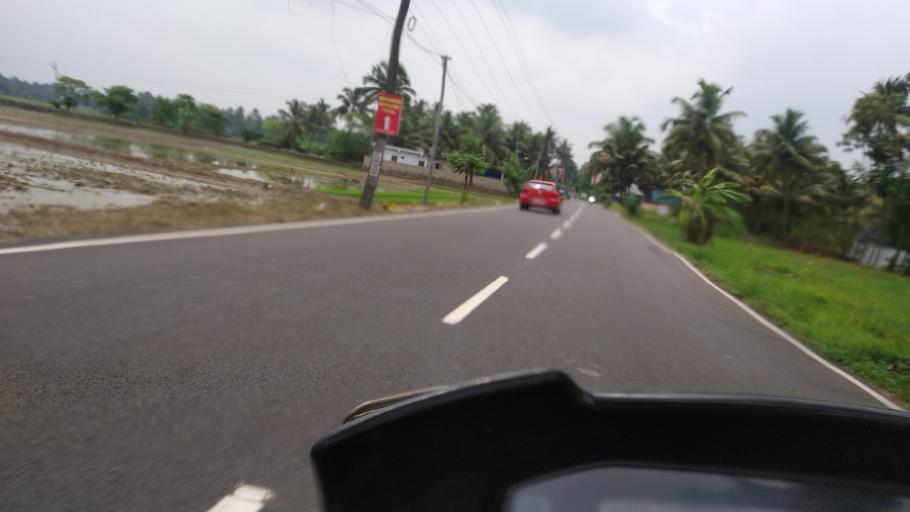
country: IN
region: Kerala
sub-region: Ernakulam
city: Aluva
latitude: 10.1560
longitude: 76.3139
